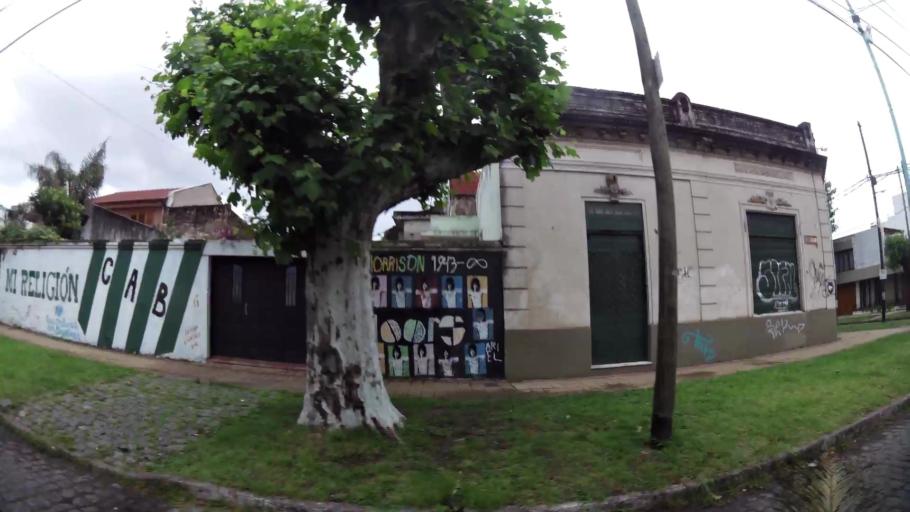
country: AR
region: Buenos Aires
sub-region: Partido de Lomas de Zamora
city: Lomas de Zamora
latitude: -34.7476
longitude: -58.3906
